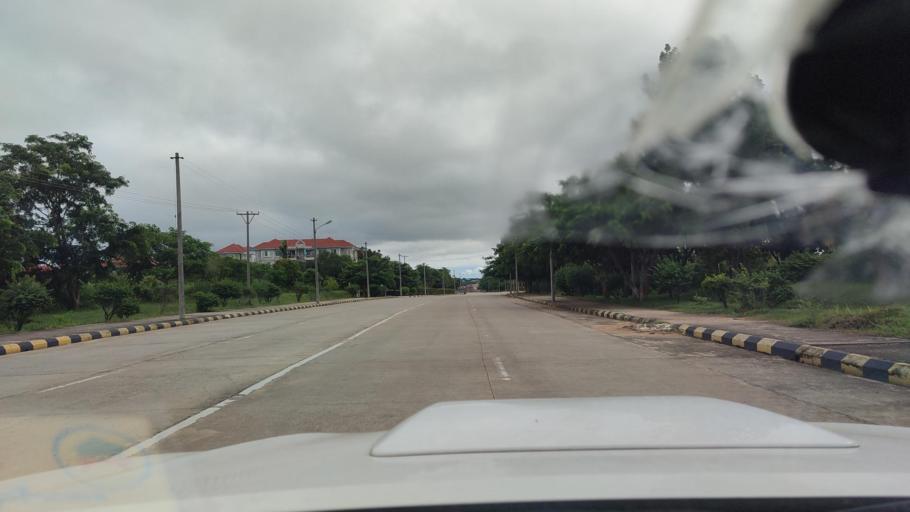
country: MM
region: Mandalay
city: Nay Pyi Taw
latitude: 19.7438
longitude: 96.0647
